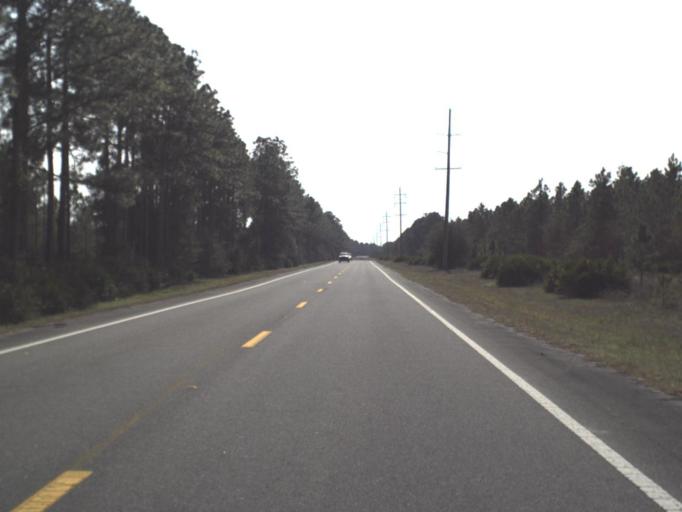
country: US
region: Florida
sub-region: Franklin County
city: Carrabelle
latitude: 29.9363
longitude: -84.5050
